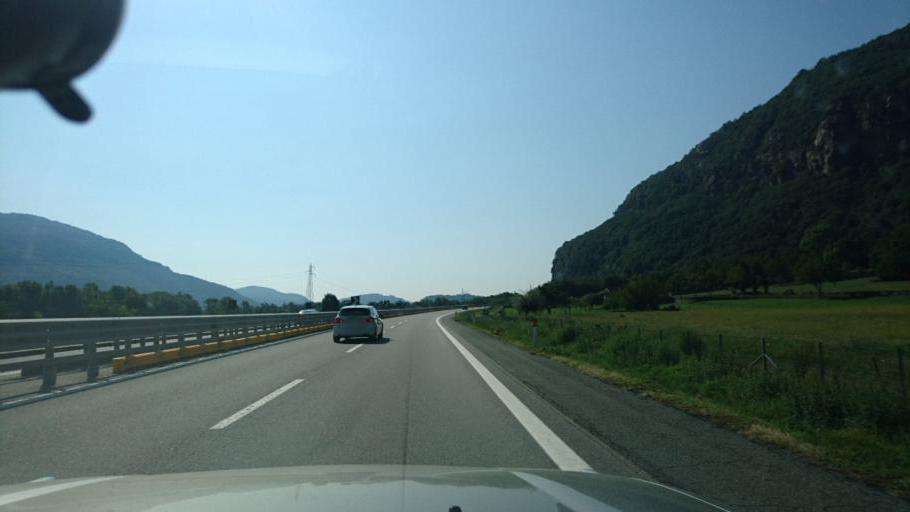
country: IT
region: Piedmont
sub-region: Provincia di Torino
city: Tavagnasco
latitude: 45.5406
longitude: 7.8274
